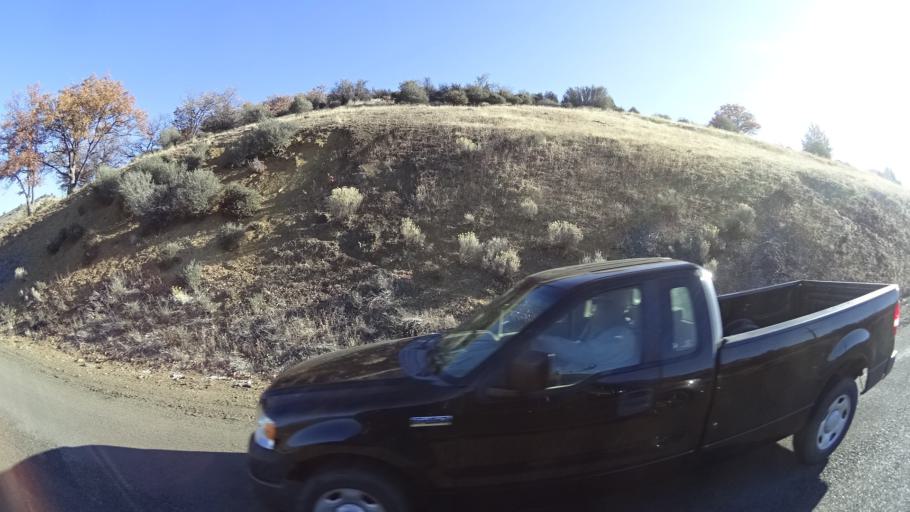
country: US
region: California
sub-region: Siskiyou County
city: Montague
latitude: 41.8781
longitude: -122.4715
